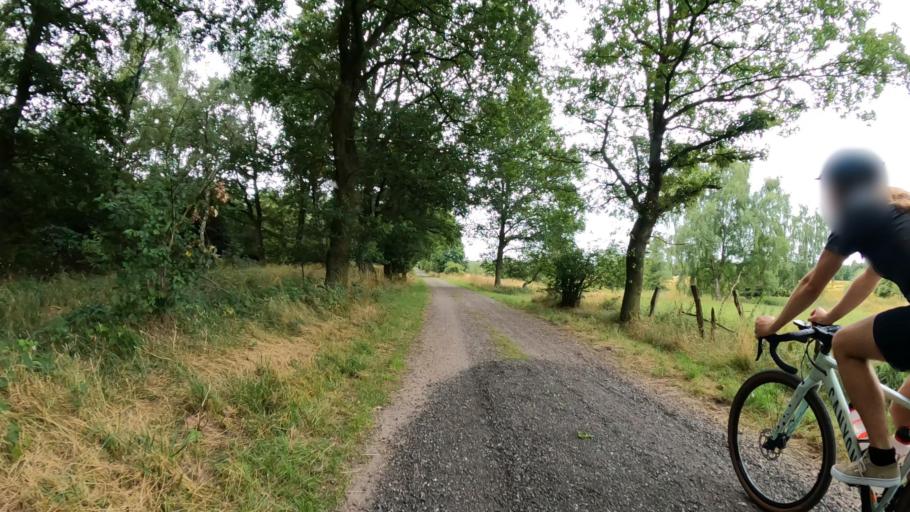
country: DE
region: Schleswig-Holstein
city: Seth
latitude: 53.8496
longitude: 10.1942
